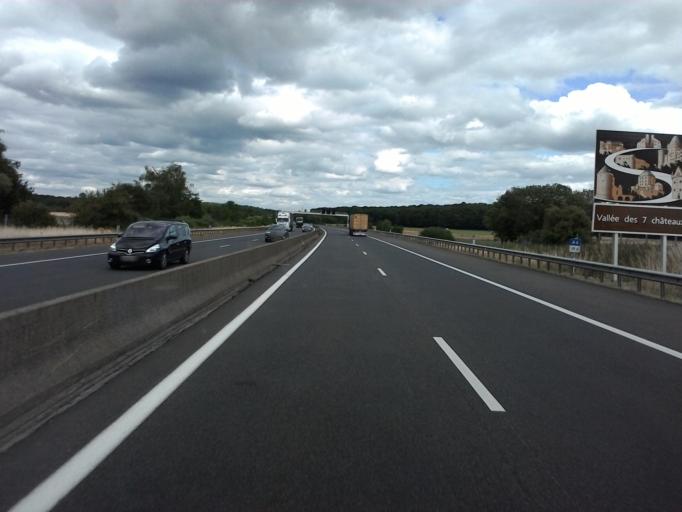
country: LU
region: Luxembourg
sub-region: Canton de Capellen
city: Steinfort
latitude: 49.6359
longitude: 5.9297
